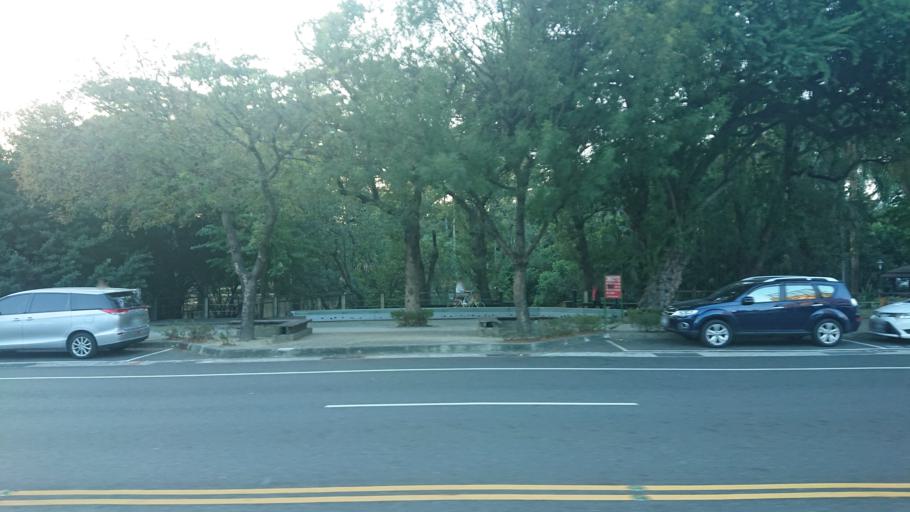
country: TW
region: Taiwan
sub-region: Tainan
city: Tainan
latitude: 23.0031
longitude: 120.2133
